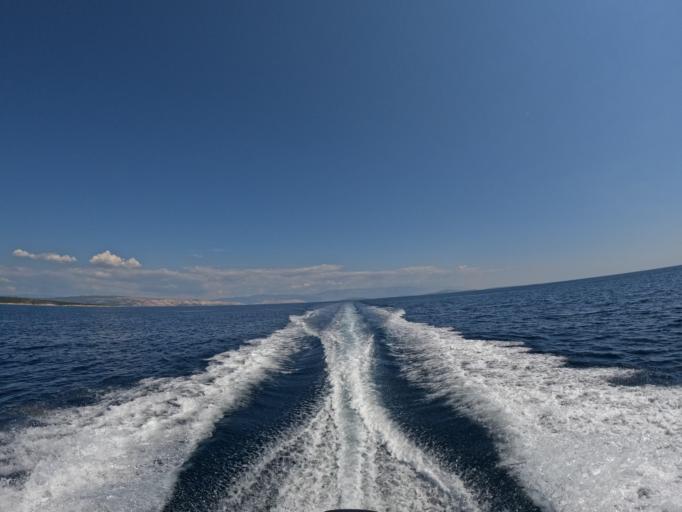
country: HR
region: Primorsko-Goranska
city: Cres
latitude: 44.9397
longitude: 14.4938
